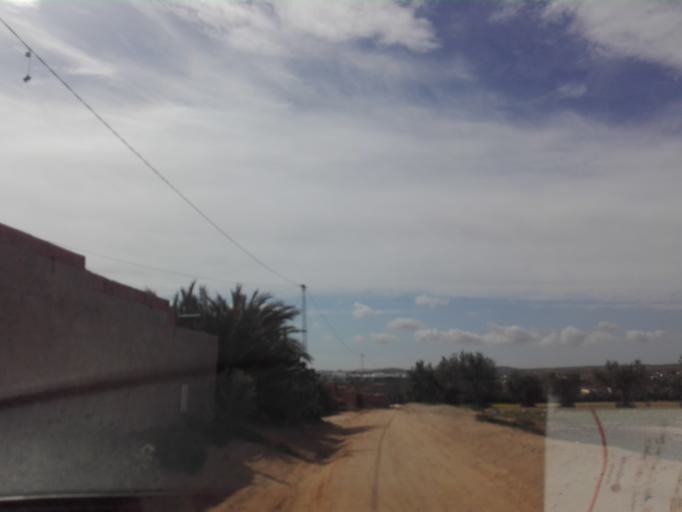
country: TN
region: Safaqis
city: Sfax
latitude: 34.7416
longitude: 10.5052
